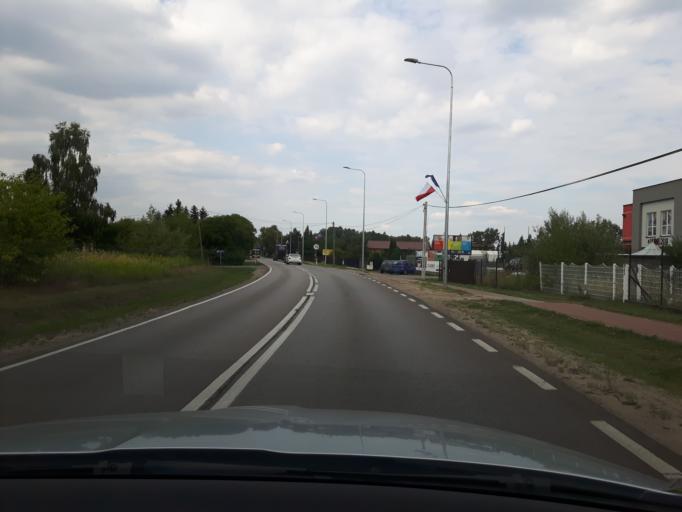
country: PL
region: Masovian Voivodeship
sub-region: Powiat legionowski
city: Nieporet
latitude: 52.4048
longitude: 21.0385
